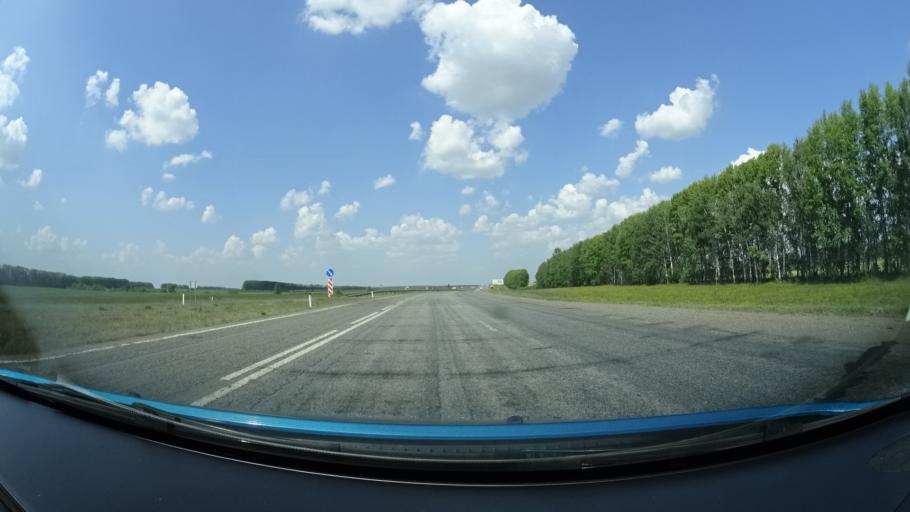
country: RU
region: Bashkortostan
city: Alekseyevka
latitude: 54.7195
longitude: 55.1836
